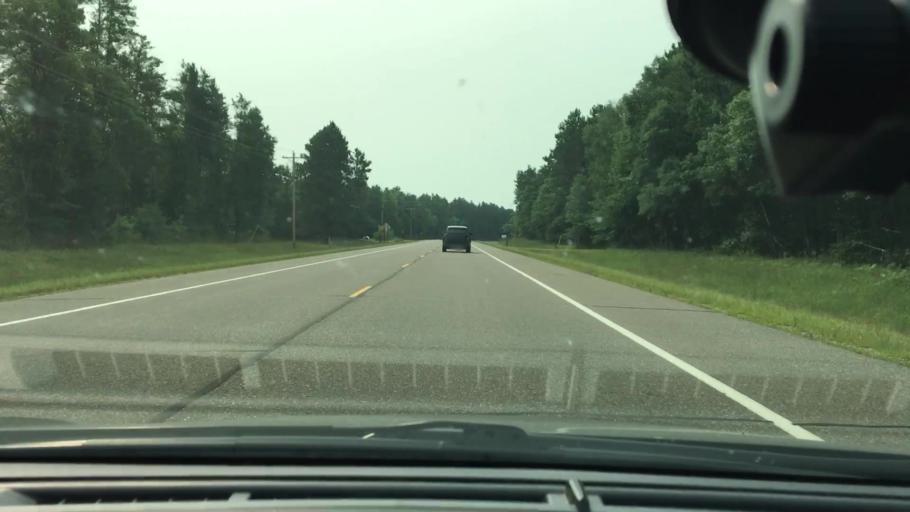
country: US
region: Minnesota
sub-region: Crow Wing County
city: Cross Lake
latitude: 46.5704
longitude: -94.1291
